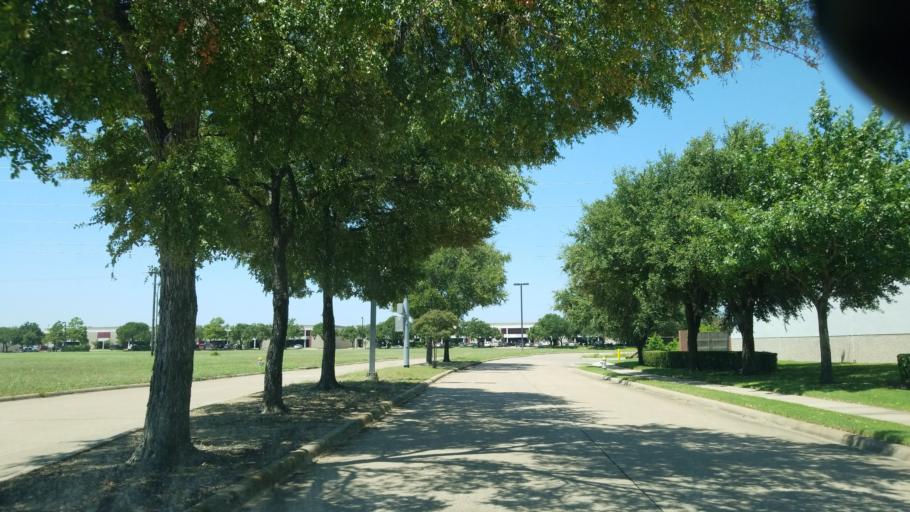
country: US
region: Texas
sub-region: Dallas County
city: Carrollton
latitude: 32.9594
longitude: -96.9182
